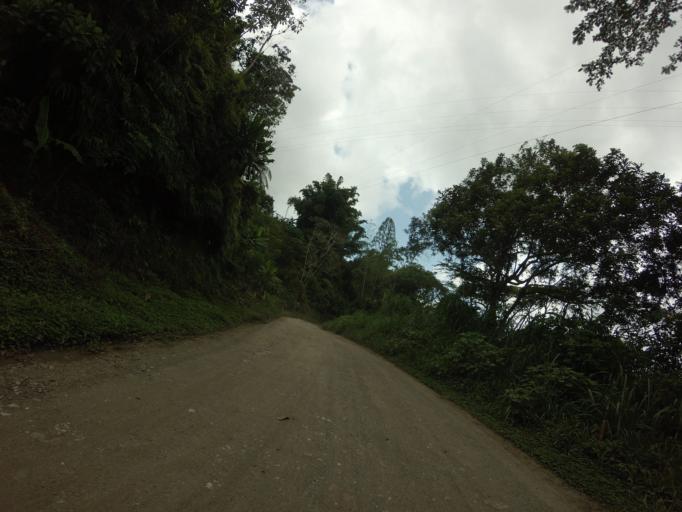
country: CO
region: Caldas
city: Victoria
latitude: 5.3108
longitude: -74.9670
